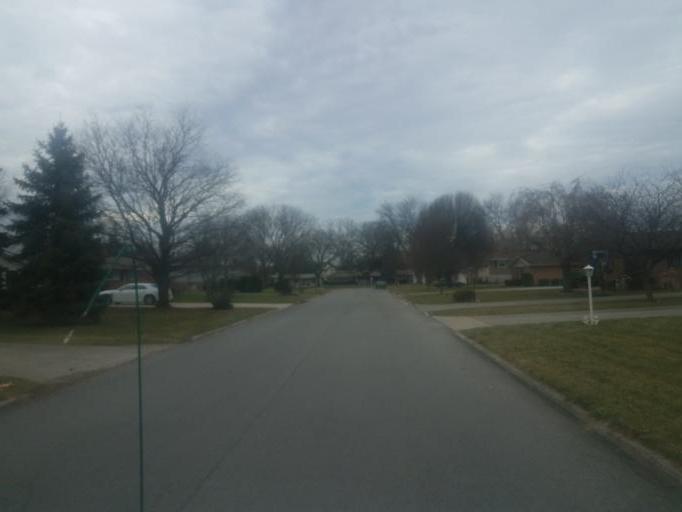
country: US
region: Ohio
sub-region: Marion County
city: Marion
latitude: 40.5754
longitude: -83.0827
